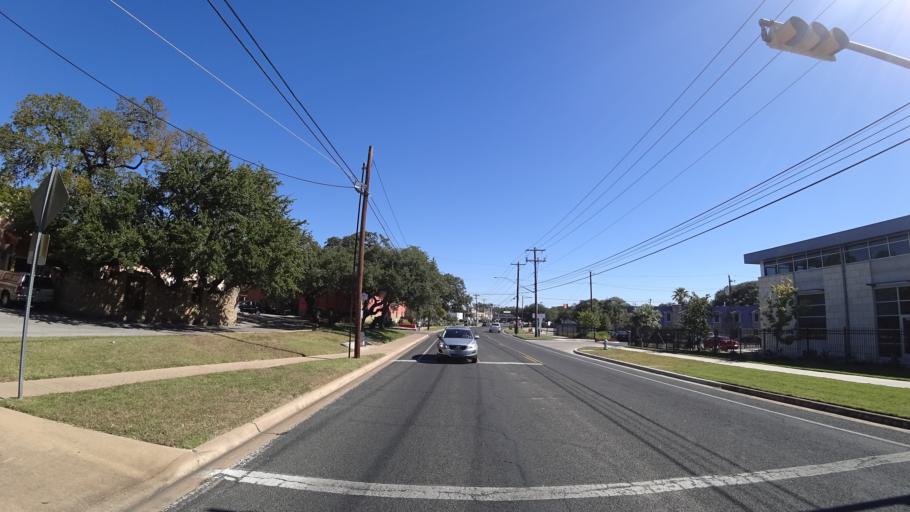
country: US
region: Texas
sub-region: Travis County
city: Austin
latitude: 30.3255
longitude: -97.7422
